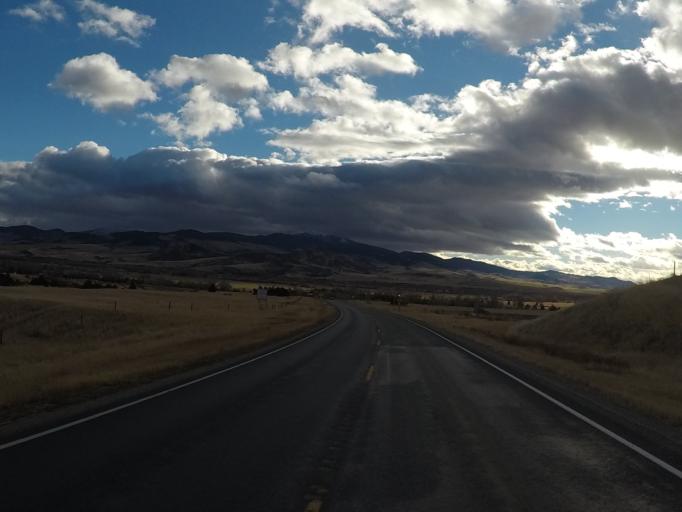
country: US
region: Montana
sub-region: Jefferson County
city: Whitehall
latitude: 45.8775
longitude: -111.9765
